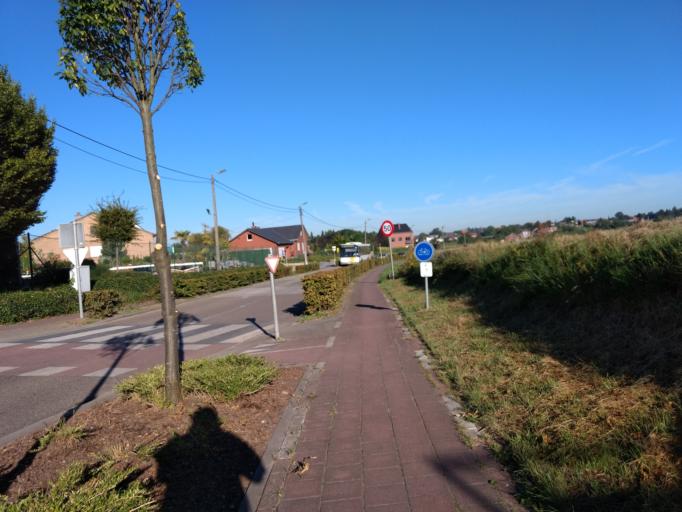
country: BE
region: Flanders
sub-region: Provincie Vlaams-Brabant
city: Bierbeek
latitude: 50.8347
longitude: 4.7398
